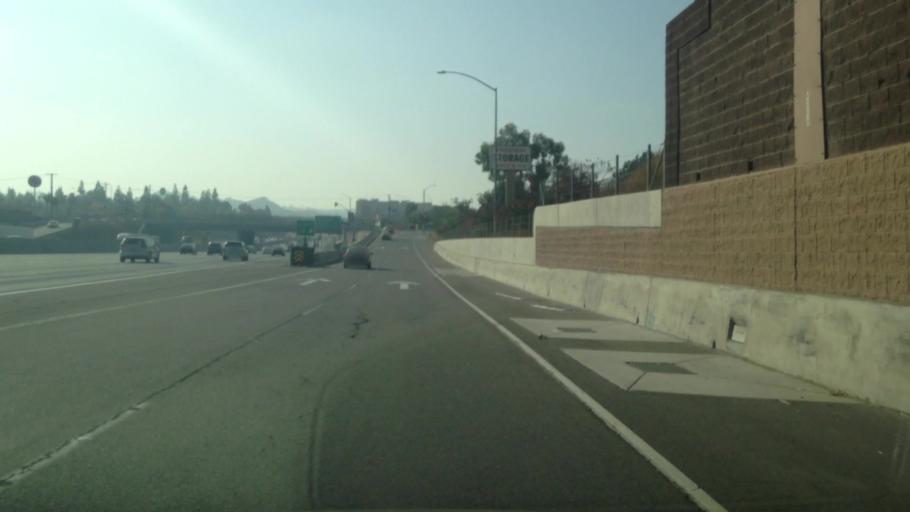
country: US
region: California
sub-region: Riverside County
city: Highgrove
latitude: 33.9849
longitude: -117.3453
